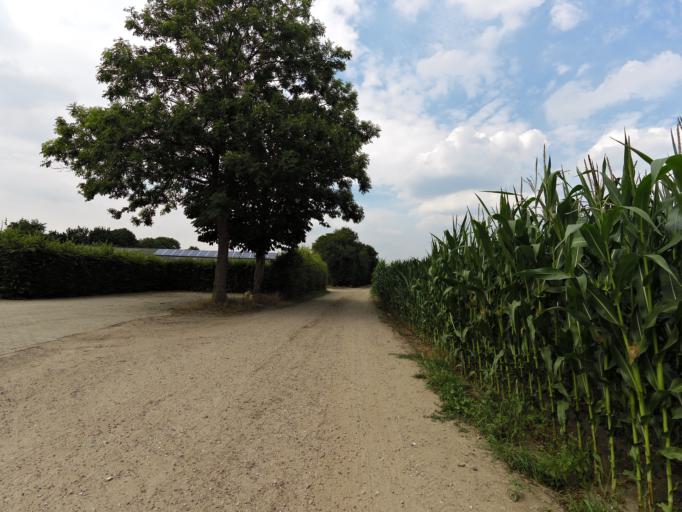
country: NL
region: Gelderland
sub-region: Gemeente Montferland
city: s-Heerenberg
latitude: 51.8817
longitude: 6.2177
